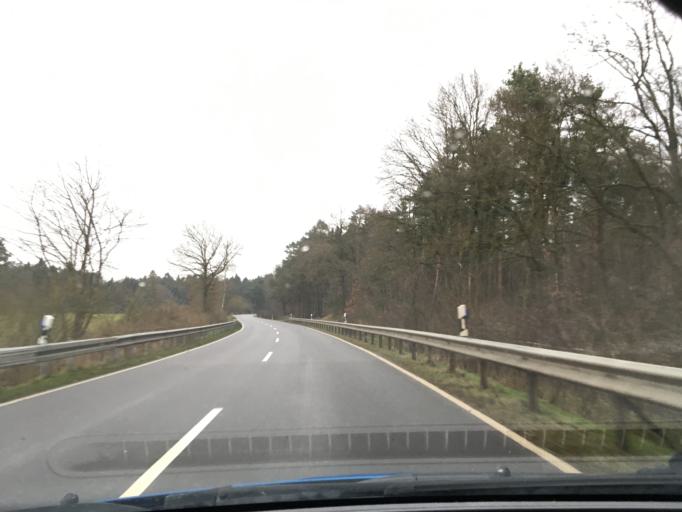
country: DE
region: Schleswig-Holstein
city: Roseburg
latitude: 53.5384
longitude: 10.6352
